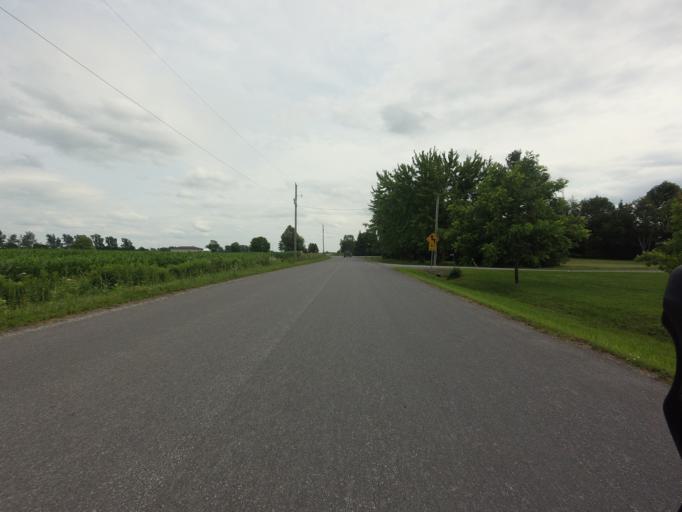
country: CA
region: Ontario
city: Bells Corners
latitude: 45.0851
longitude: -75.5958
